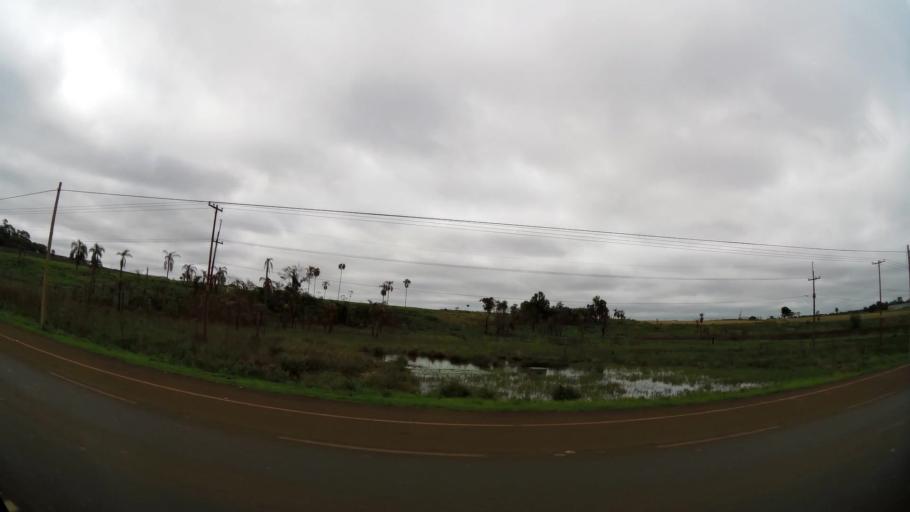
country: PY
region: Alto Parana
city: Colonia Yguazu
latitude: -25.4879
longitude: -54.8293
